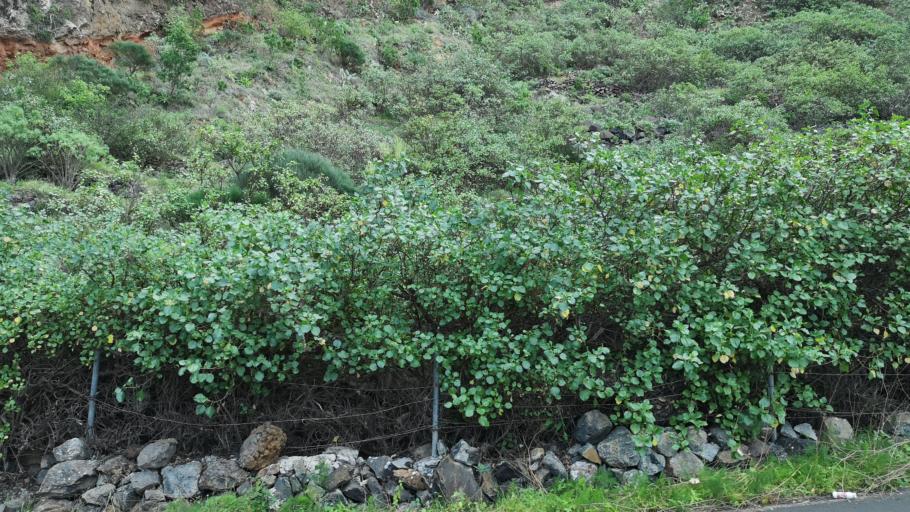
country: ES
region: Canary Islands
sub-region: Provincia de Santa Cruz de Tenerife
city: Agulo
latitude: 28.1913
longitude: -17.1980
